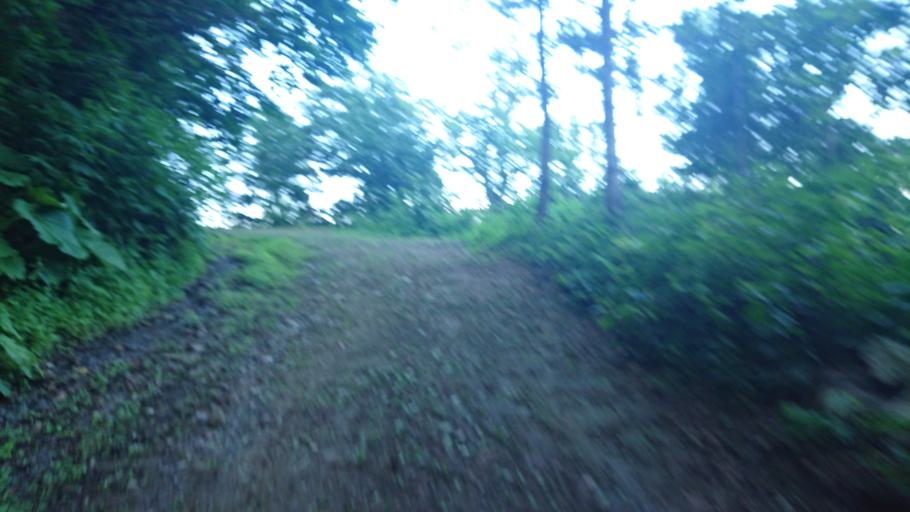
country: TR
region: Rize
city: Rize
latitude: 40.9740
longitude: 40.4972
